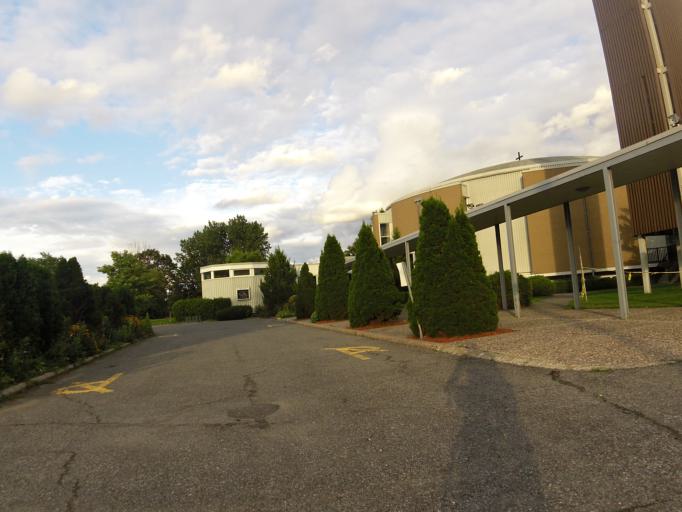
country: CA
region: Ontario
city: Ottawa
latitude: 45.3719
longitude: -75.7546
